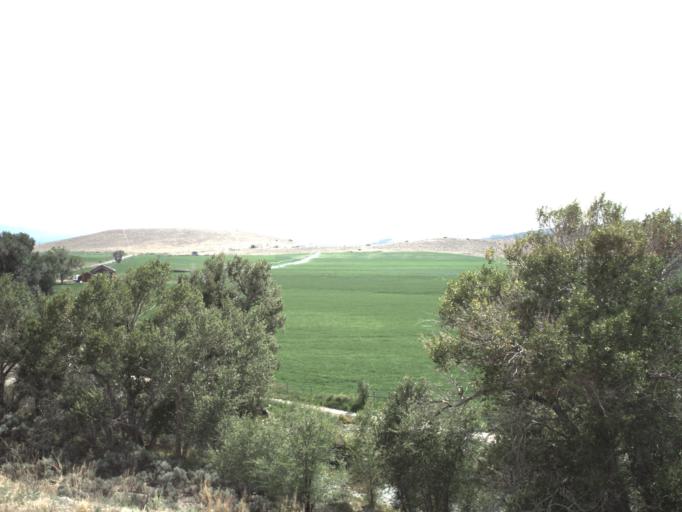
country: US
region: Utah
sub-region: Piute County
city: Junction
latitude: 38.0937
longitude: -111.9833
